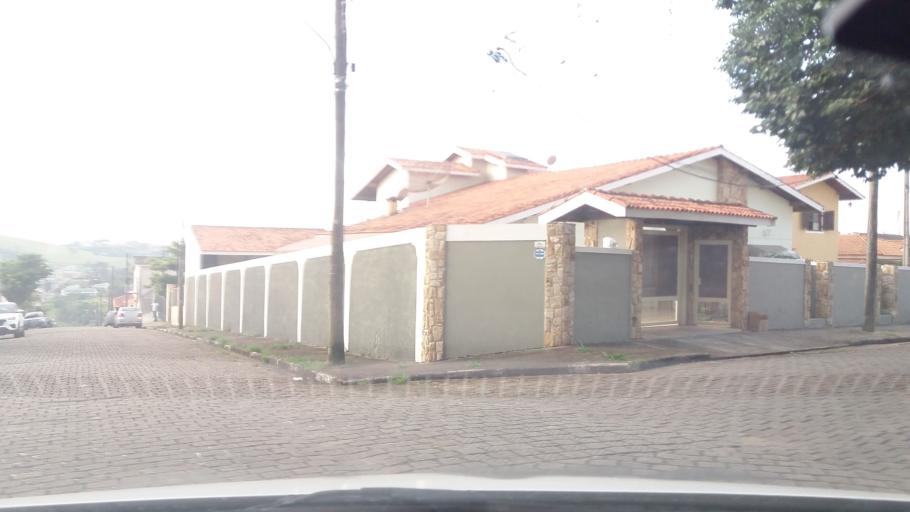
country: BR
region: Sao Paulo
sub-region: Bom Jesus Dos Perdoes
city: Bom Jesus dos Perdoes
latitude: -23.1421
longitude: -46.4644
